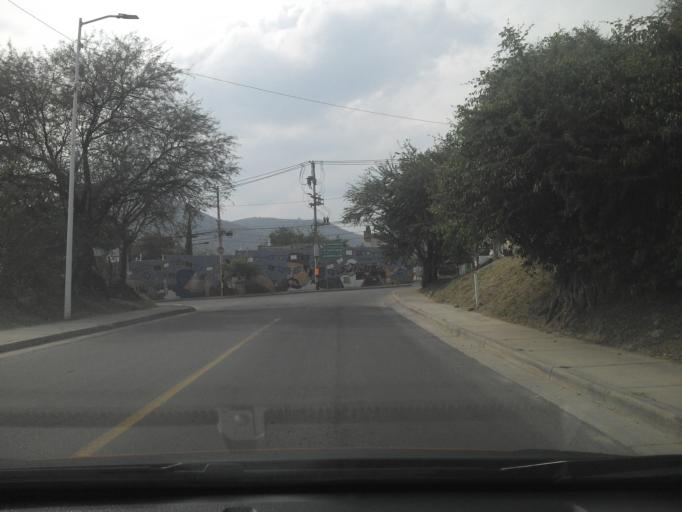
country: MX
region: Jalisco
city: Tlajomulco de Zuniga
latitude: 20.4767
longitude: -103.4424
